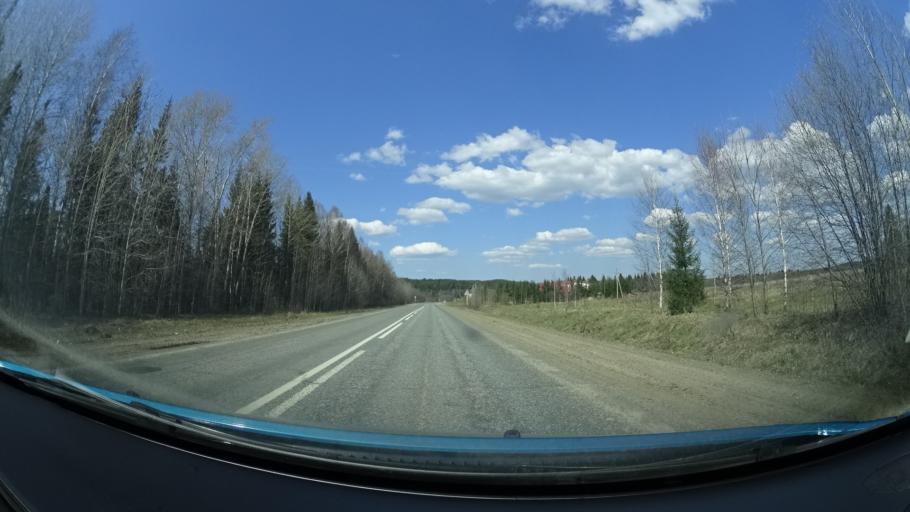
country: RU
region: Perm
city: Yugo-Kamskiy
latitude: 57.5388
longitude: 55.6872
